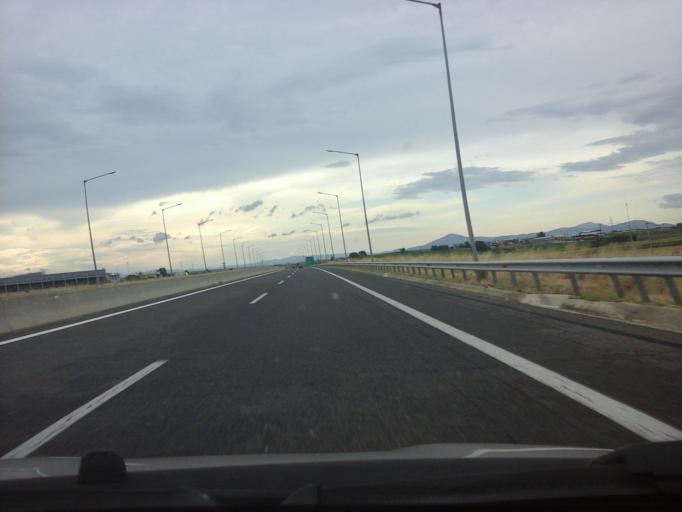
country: GR
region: East Macedonia and Thrace
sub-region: Nomos Rodopis
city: Komotini
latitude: 41.1078
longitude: 25.3432
